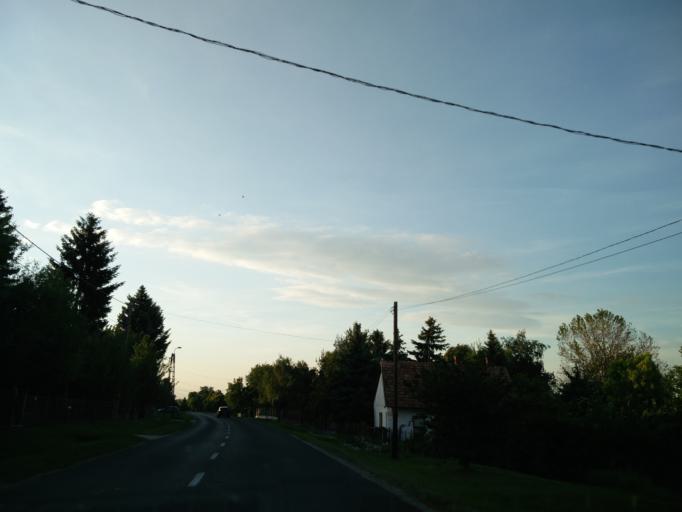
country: HU
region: Fejer
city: Lovasbereny
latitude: 47.3607
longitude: 18.5808
